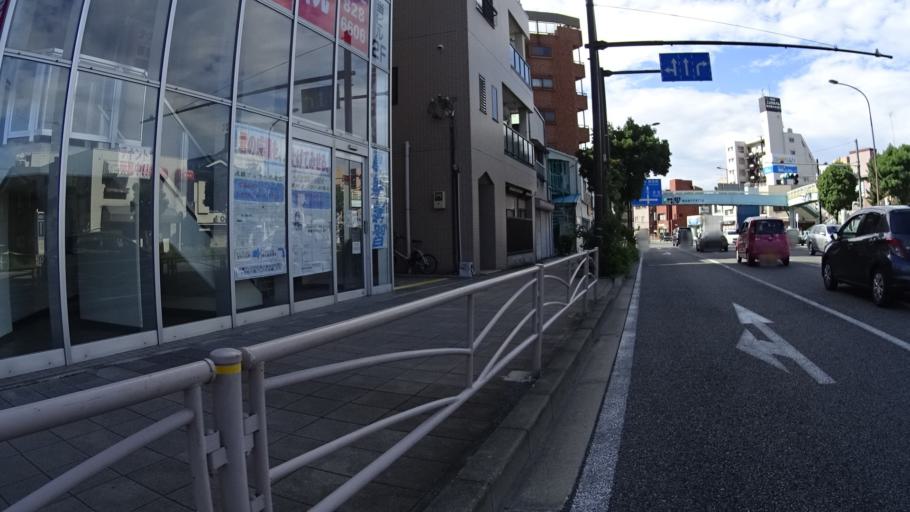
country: JP
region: Kanagawa
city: Yokosuka
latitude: 35.2735
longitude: 139.6770
